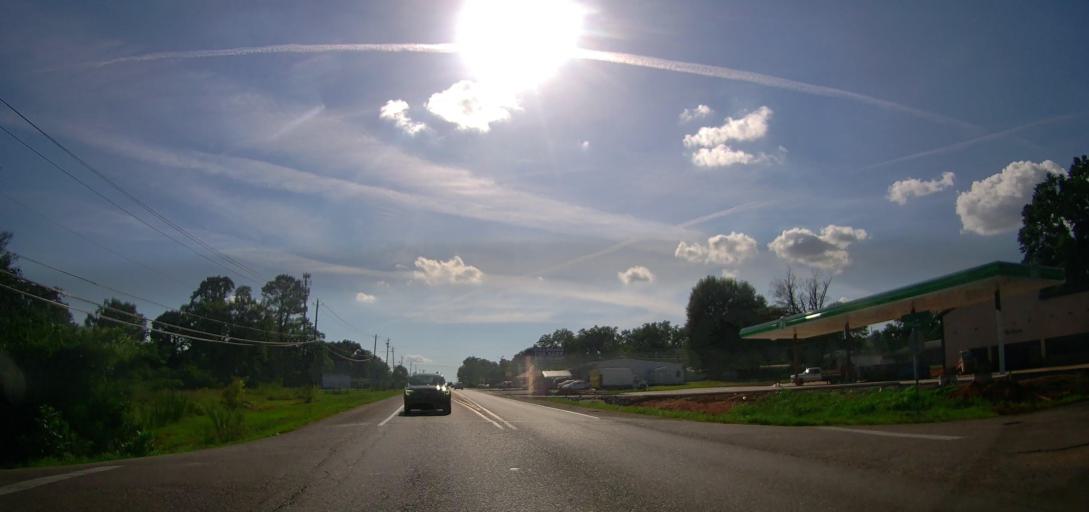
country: US
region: Alabama
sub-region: Tuscaloosa County
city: Holt
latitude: 33.1900
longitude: -87.4451
